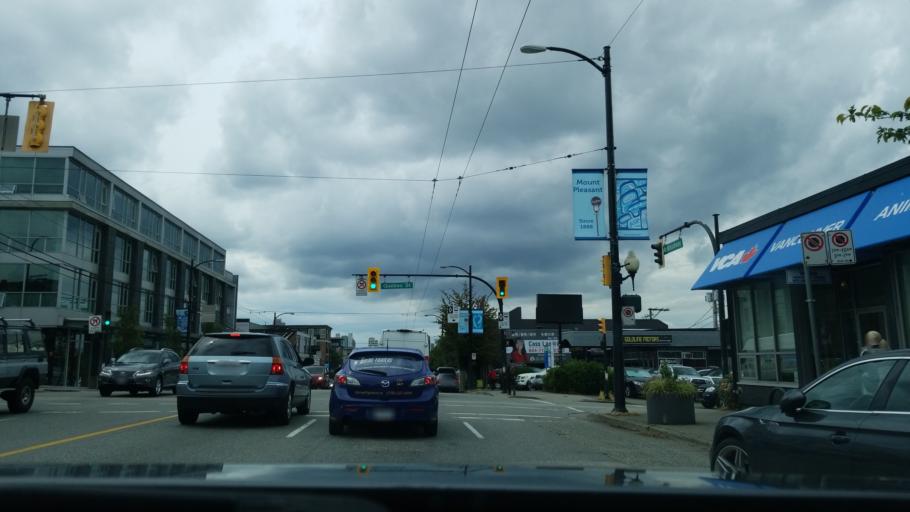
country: CA
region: British Columbia
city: Vancouver
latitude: 49.2629
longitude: -123.1020
